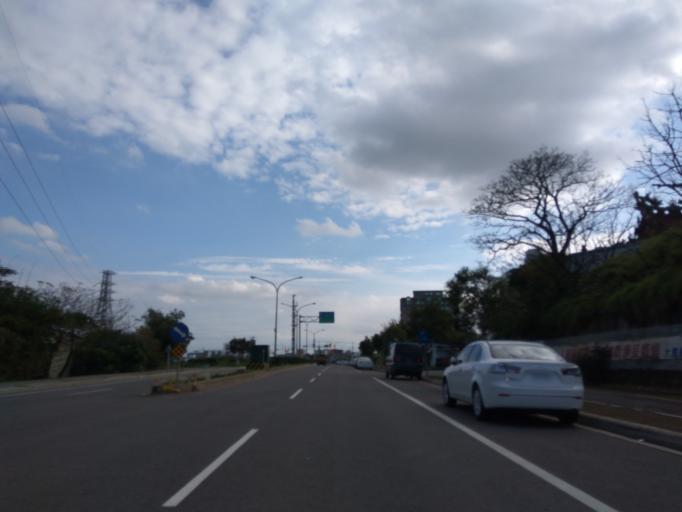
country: TW
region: Taiwan
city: Taoyuan City
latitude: 25.0643
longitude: 121.1763
